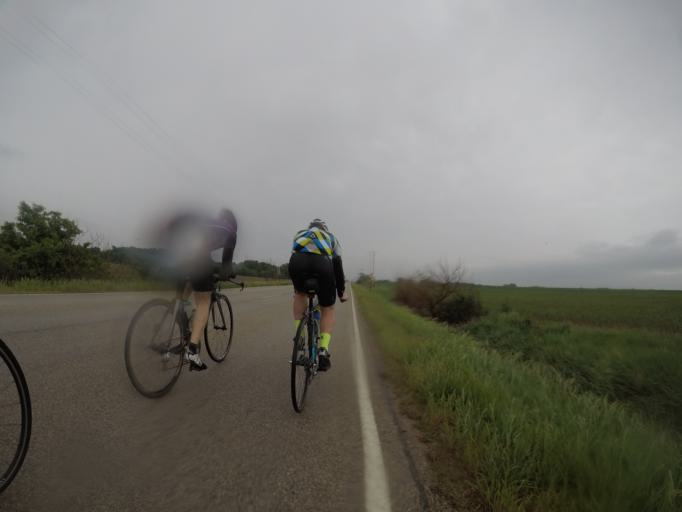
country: US
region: Kansas
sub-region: Pottawatomie County
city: Wamego
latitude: 39.3405
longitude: -96.2213
